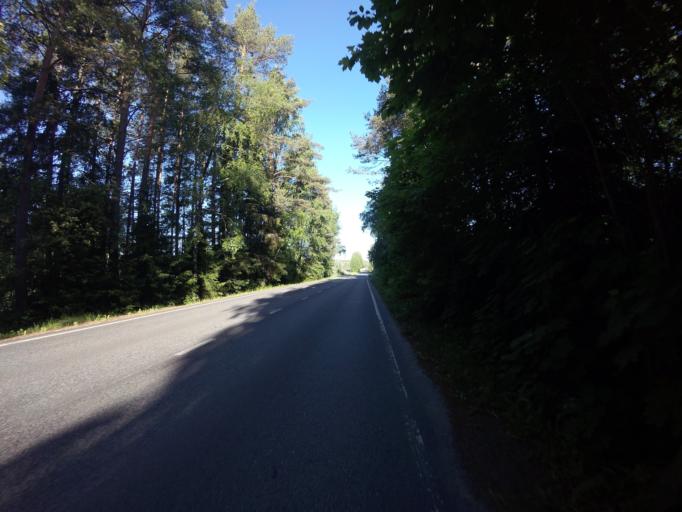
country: FI
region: Varsinais-Suomi
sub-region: Turku
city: Vahto
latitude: 60.5380
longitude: 22.3591
